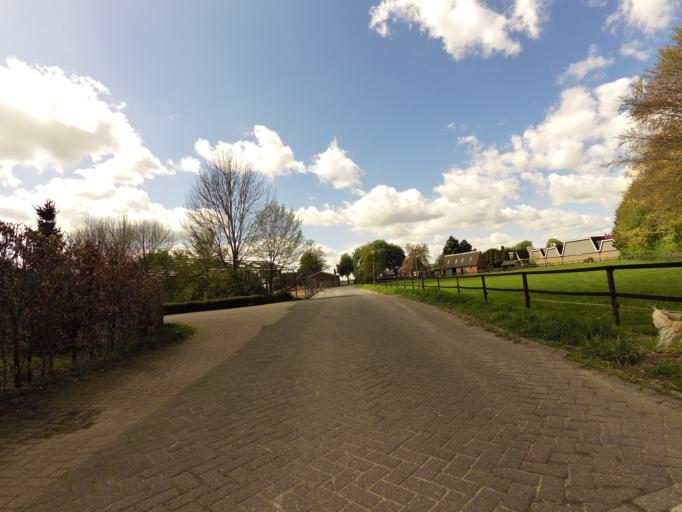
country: NL
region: Gelderland
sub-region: Gemeente Doetinchem
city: Doetinchem
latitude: 51.9408
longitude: 6.2295
